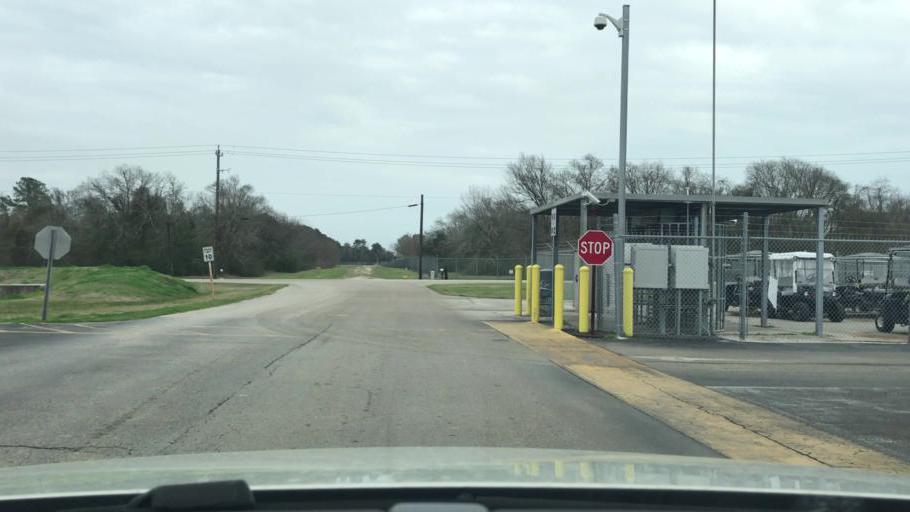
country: US
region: Texas
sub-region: Harris County
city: Baytown
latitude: 29.7650
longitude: -94.9131
